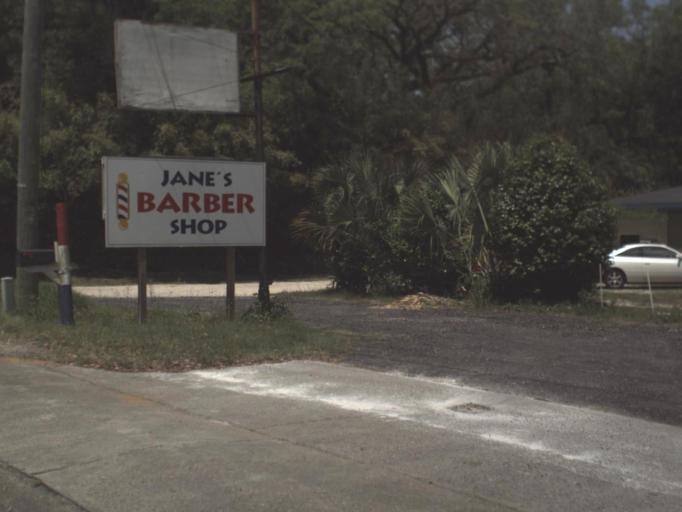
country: US
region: Florida
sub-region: Escambia County
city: West Pensacola
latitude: 30.4317
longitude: -87.2932
